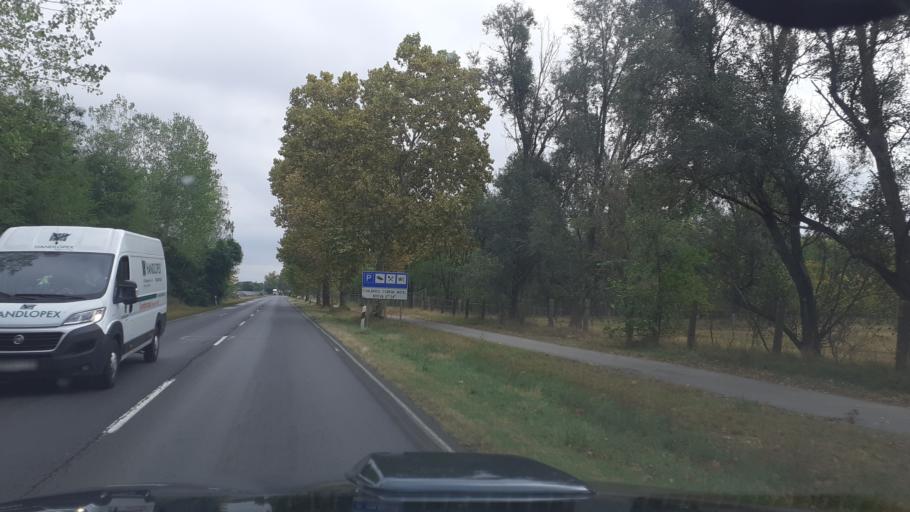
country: HU
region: Bacs-Kiskun
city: Balloszog
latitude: 46.8885
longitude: 19.5875
